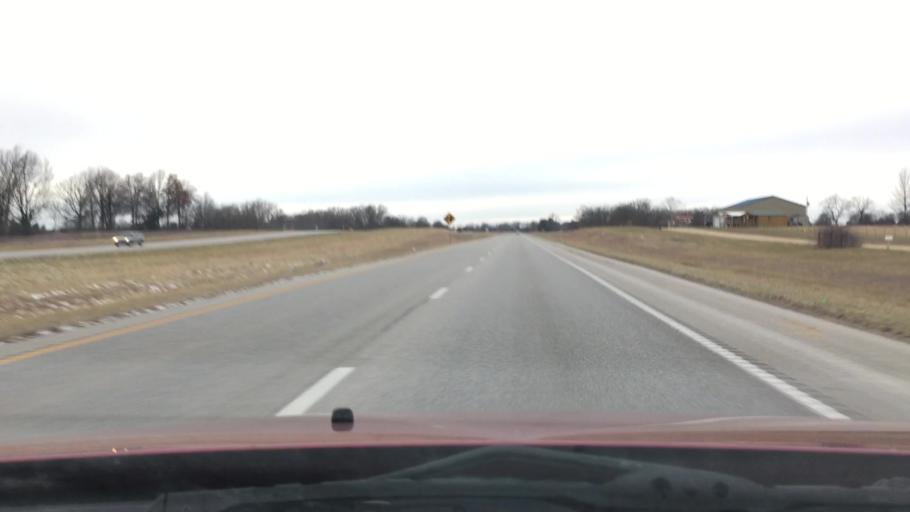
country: US
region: Missouri
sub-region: Webster County
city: Seymour
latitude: 37.1608
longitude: -92.7940
